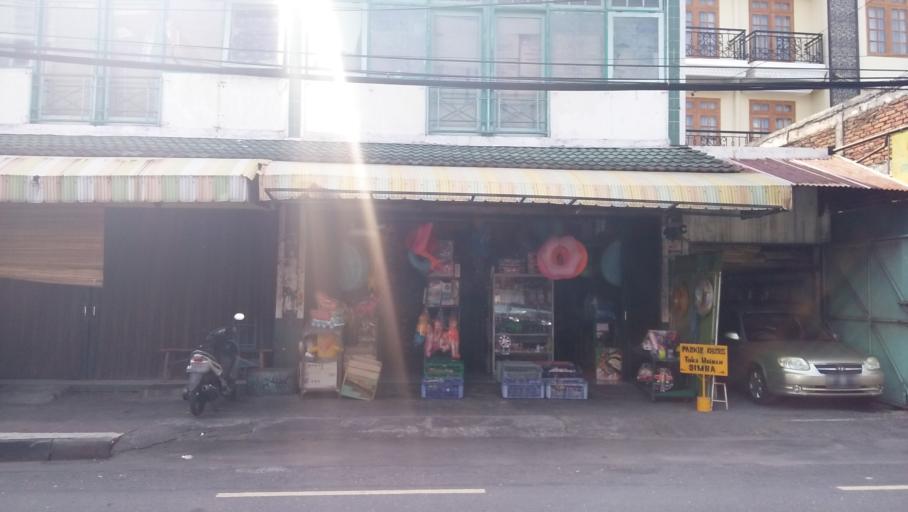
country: ID
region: Daerah Istimewa Yogyakarta
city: Yogyakarta
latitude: -7.7913
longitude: 110.3617
